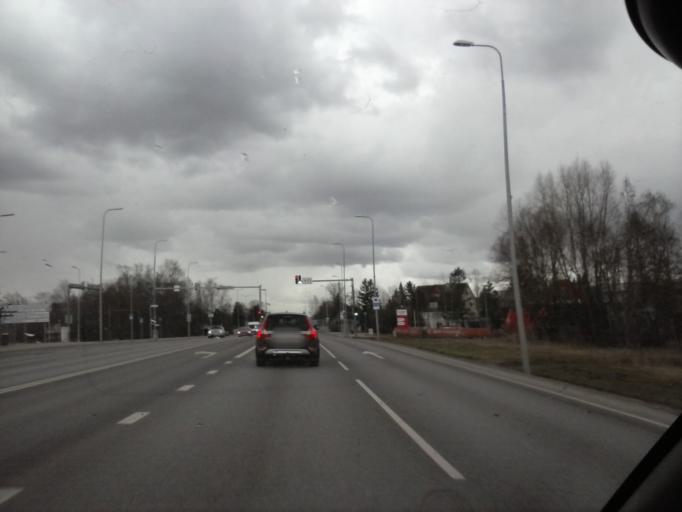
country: EE
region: Harju
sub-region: Tallinna linn
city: Tallinn
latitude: 59.4086
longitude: 24.8056
